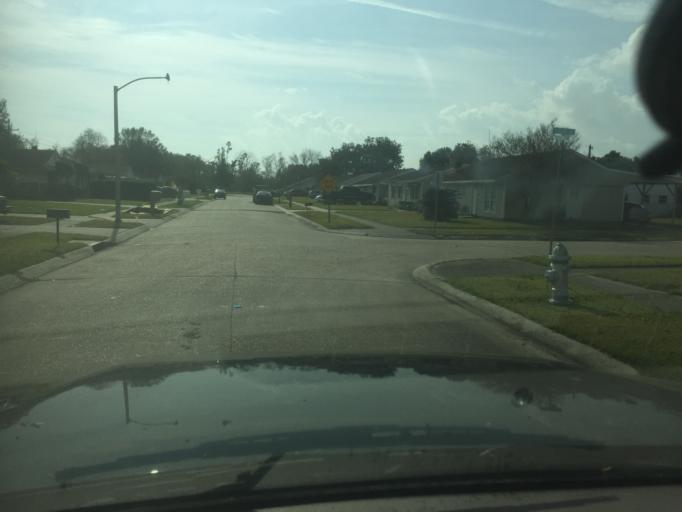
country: US
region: Louisiana
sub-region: Jefferson Parish
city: Avondale
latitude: 29.9147
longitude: -90.1994
